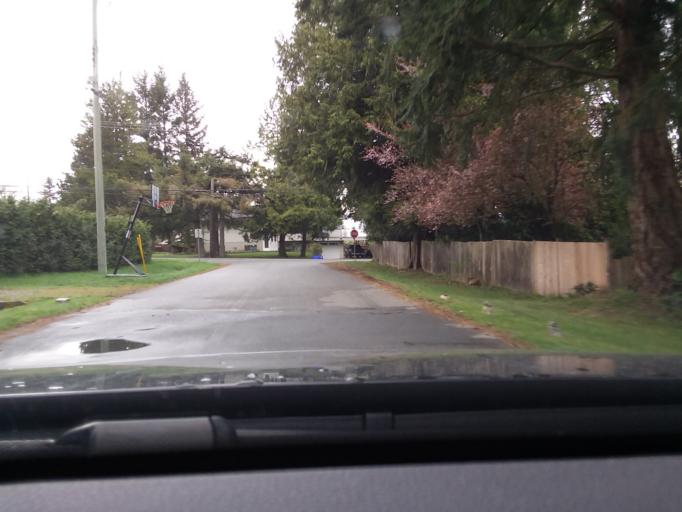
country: CA
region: British Columbia
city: North Saanich
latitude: 48.5539
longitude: -123.3972
